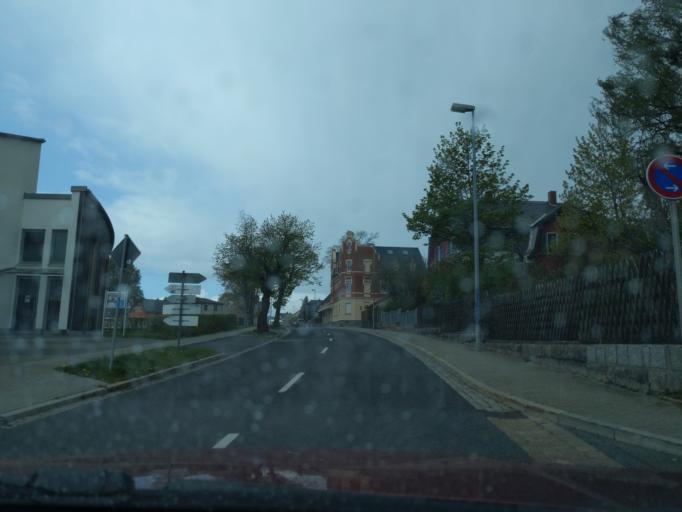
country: DE
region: Saxony
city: Schoenheide
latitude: 50.5053
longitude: 12.5165
